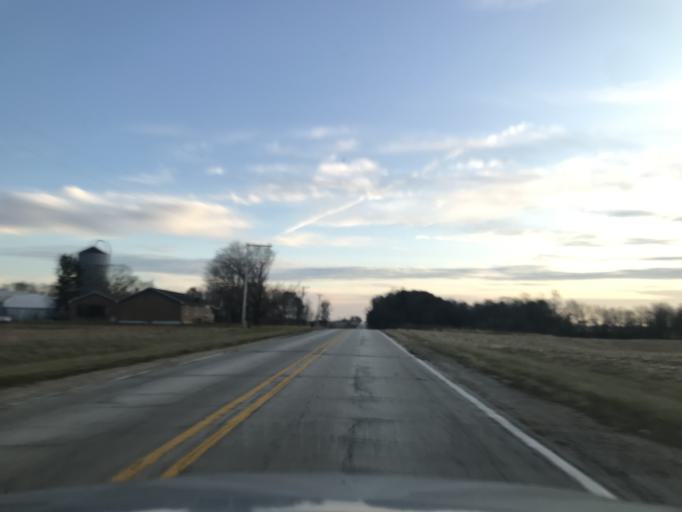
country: US
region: Illinois
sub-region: Henderson County
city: Oquawka
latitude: 40.9557
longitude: -90.8641
